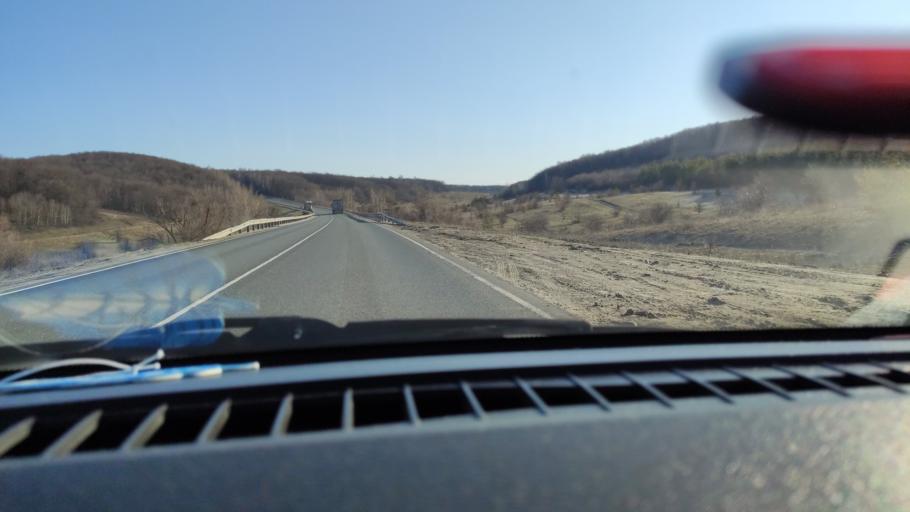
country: RU
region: Saratov
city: Alekseyevka
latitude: 52.4093
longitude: 48.0031
